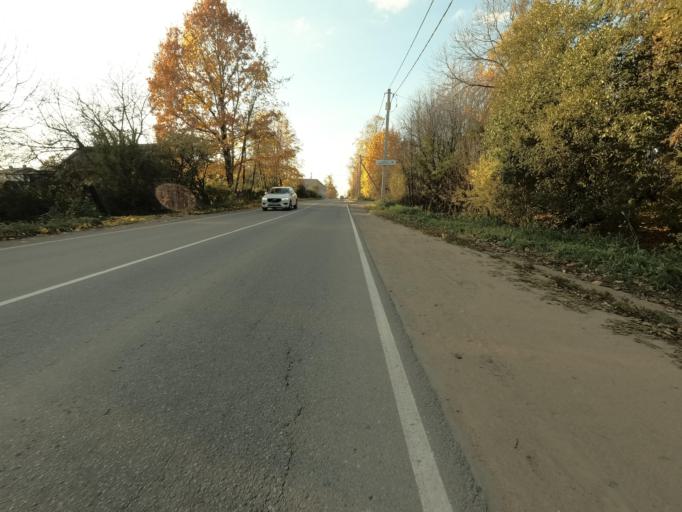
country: RU
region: Leningrad
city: Mga
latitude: 59.7501
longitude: 31.0539
